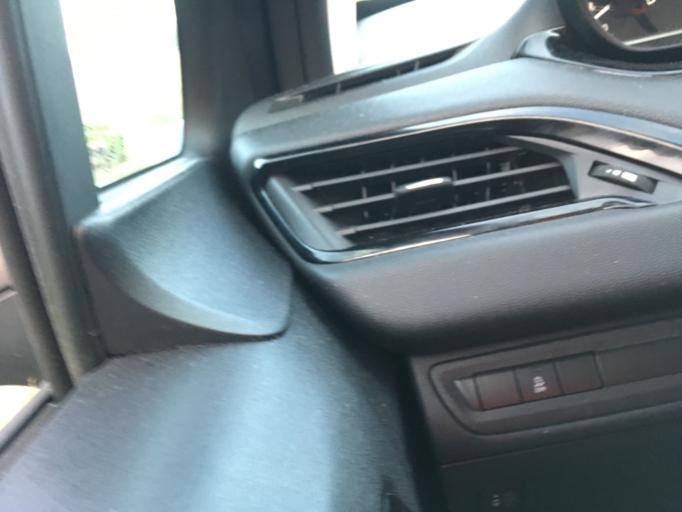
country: FR
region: Aquitaine
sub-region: Departement de la Gironde
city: Saint-Ciers-sur-Gironde
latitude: 45.3025
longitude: -0.5984
